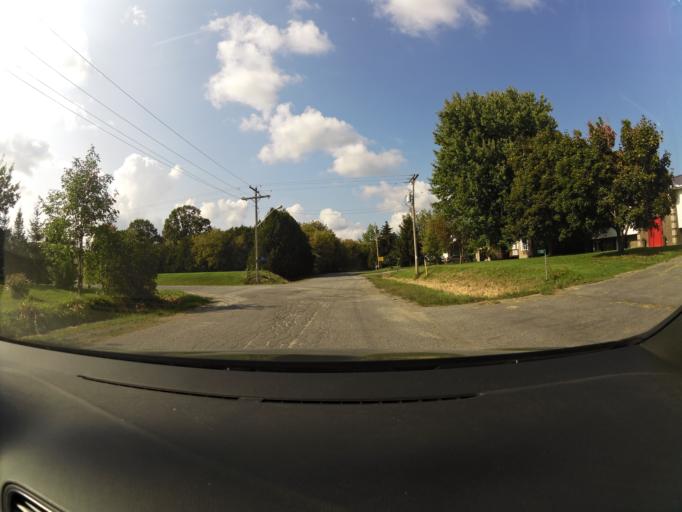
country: CA
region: Ontario
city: Arnprior
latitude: 45.3905
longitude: -76.1855
